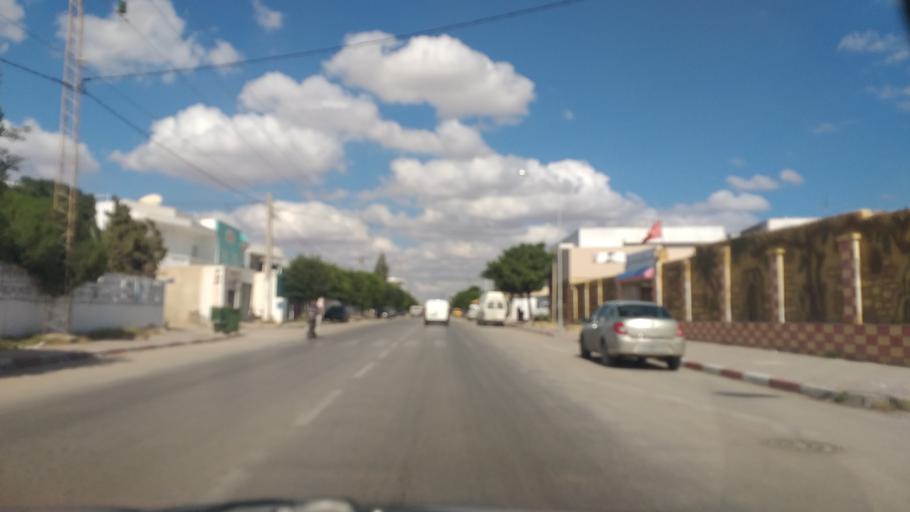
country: TN
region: Safaqis
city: Al Qarmadah
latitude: 34.7713
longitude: 10.7750
